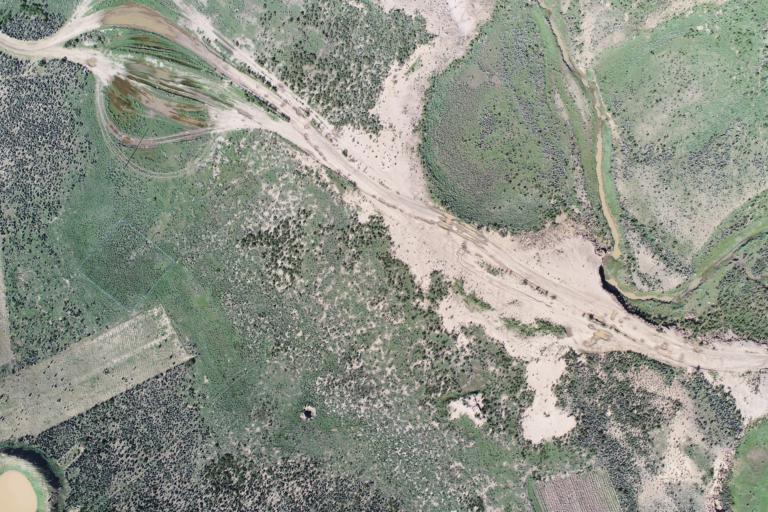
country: BO
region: La Paz
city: Curahuara de Carangas
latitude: -17.3034
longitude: -68.5217
